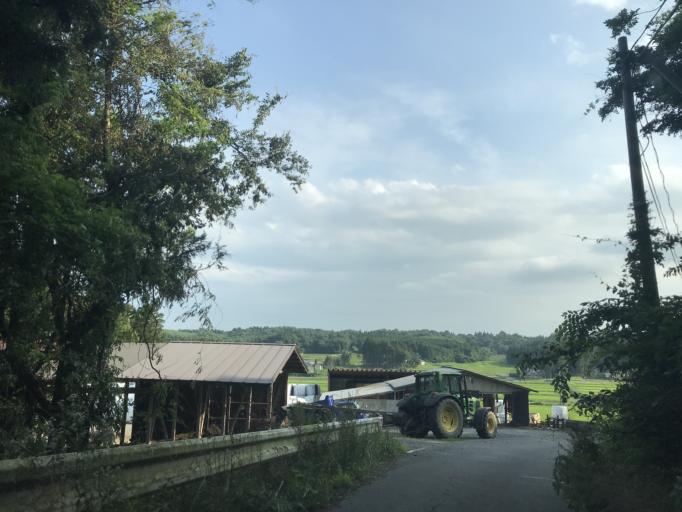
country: JP
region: Iwate
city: Ichinoseki
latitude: 38.8485
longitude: 141.1144
